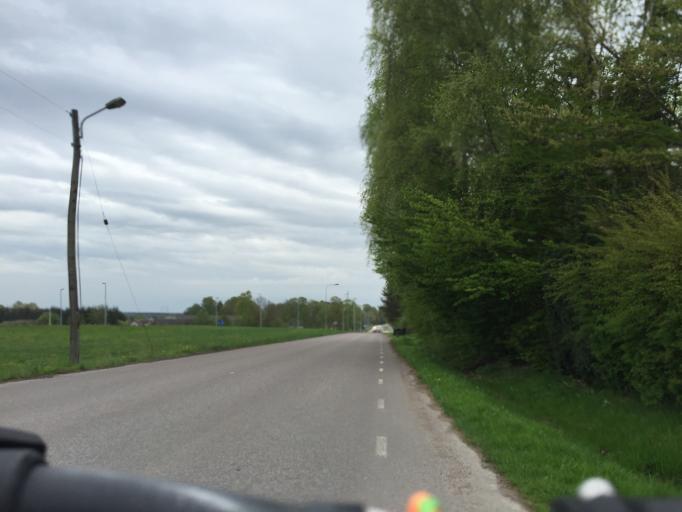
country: SE
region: Skane
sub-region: Lunds Kommun
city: Veberod
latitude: 55.6448
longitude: 13.4694
